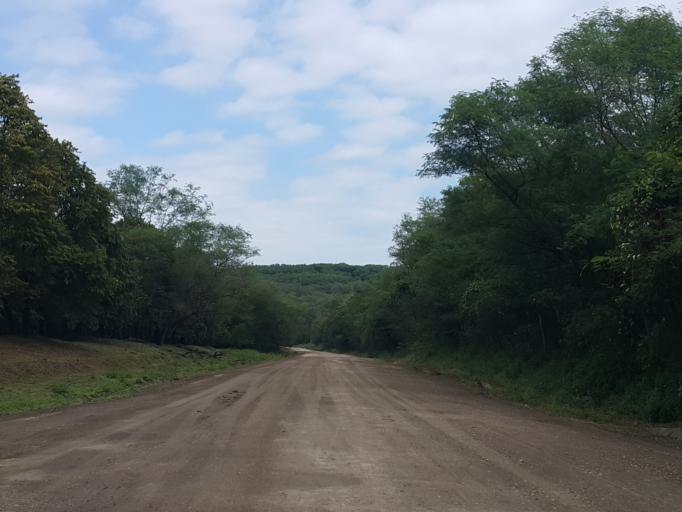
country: TH
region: Lampang
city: Mae Mo
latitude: 18.3216
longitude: 99.7498
